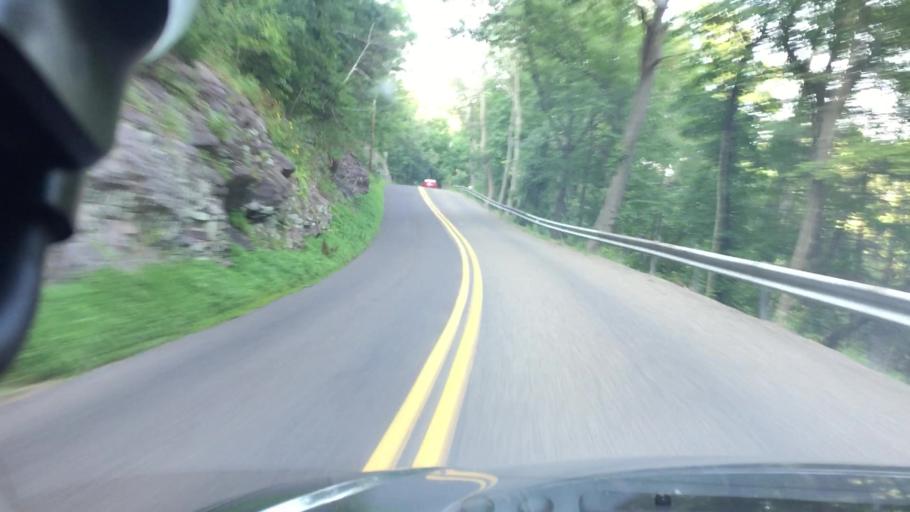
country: US
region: Pennsylvania
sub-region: Columbia County
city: Espy
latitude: 40.9769
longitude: -76.3973
